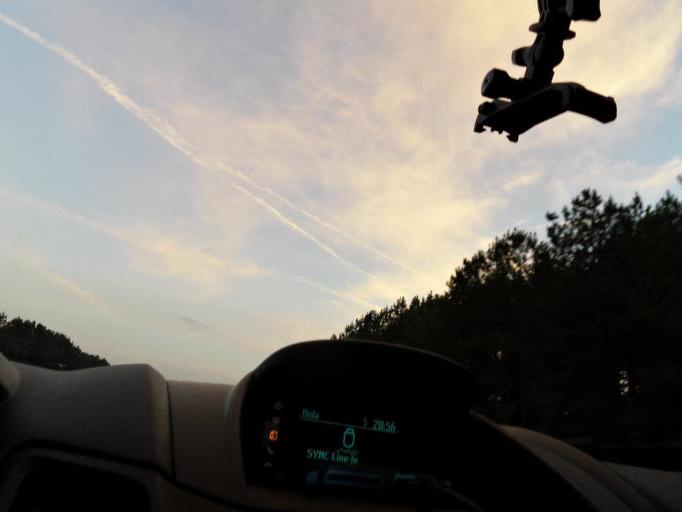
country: US
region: Mississippi
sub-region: Lauderdale County
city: Meridian Station
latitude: 32.6661
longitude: -88.4924
